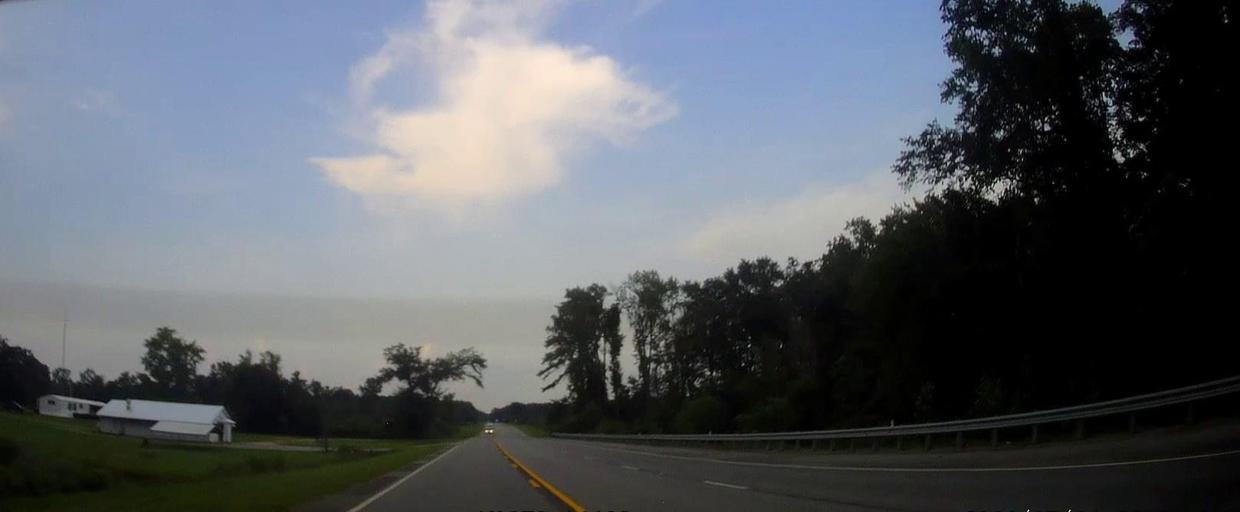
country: US
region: Georgia
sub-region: Laurens County
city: East Dublin
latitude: 32.6080
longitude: -82.8195
